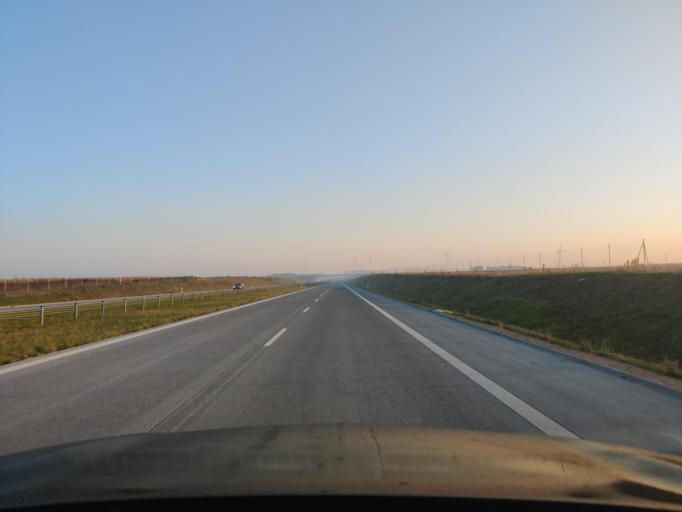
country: PL
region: Masovian Voivodeship
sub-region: Powiat mlawski
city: Wisniewo
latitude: 53.0203
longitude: 20.3414
